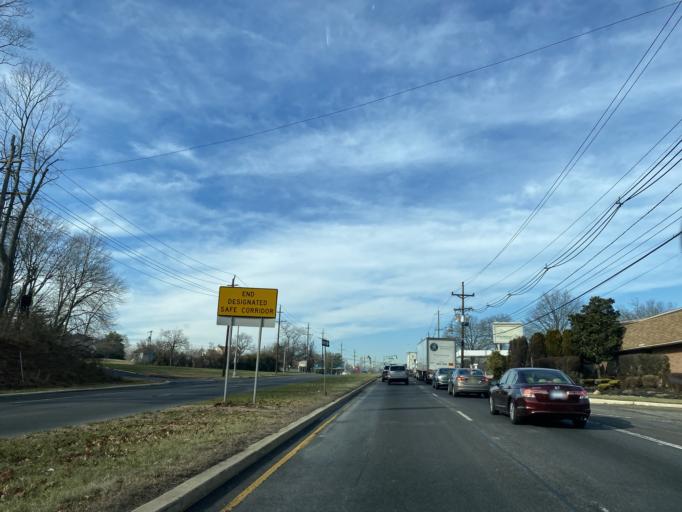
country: US
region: New Jersey
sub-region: Burlington County
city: Maple Shade
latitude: 39.9630
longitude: -74.9954
